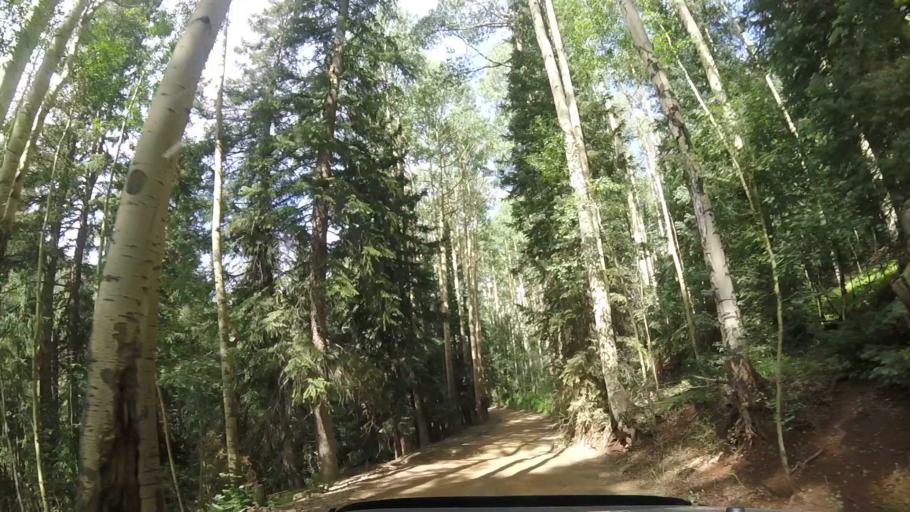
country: US
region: Colorado
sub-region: San Miguel County
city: Telluride
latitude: 37.8575
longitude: -107.8194
